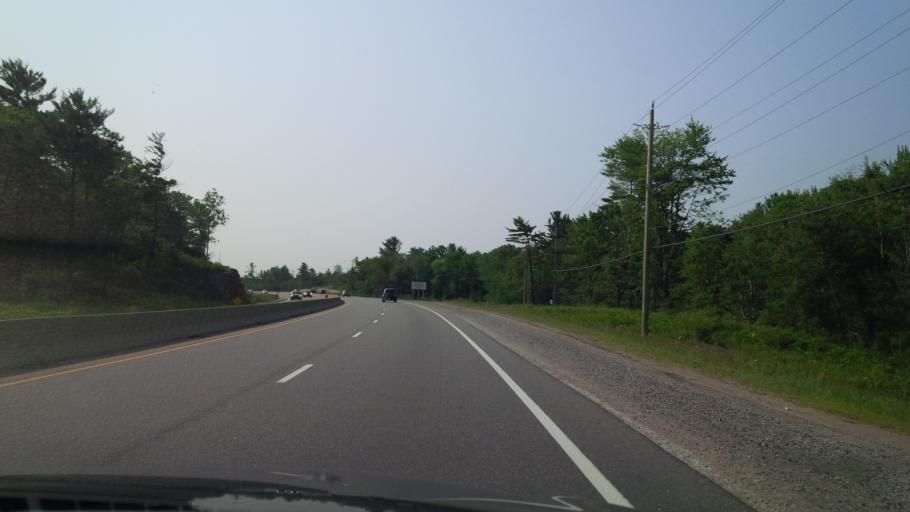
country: CA
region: Ontario
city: Gravenhurst
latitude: 44.8989
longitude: -79.3651
